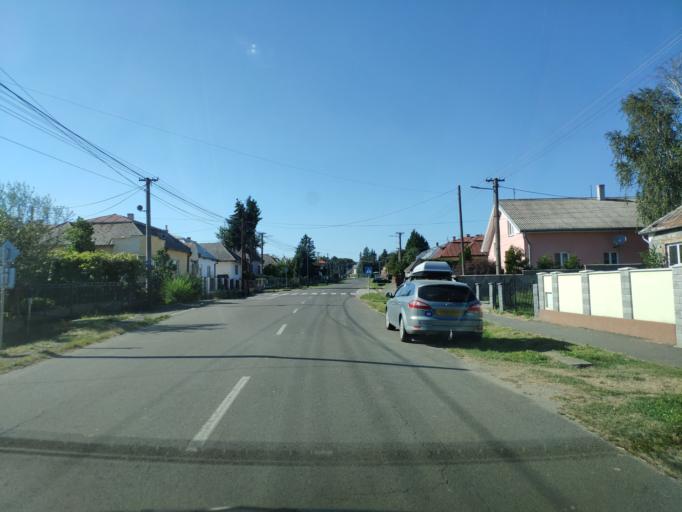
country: SK
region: Kosicky
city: Trebisov
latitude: 48.5768
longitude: 21.8529
